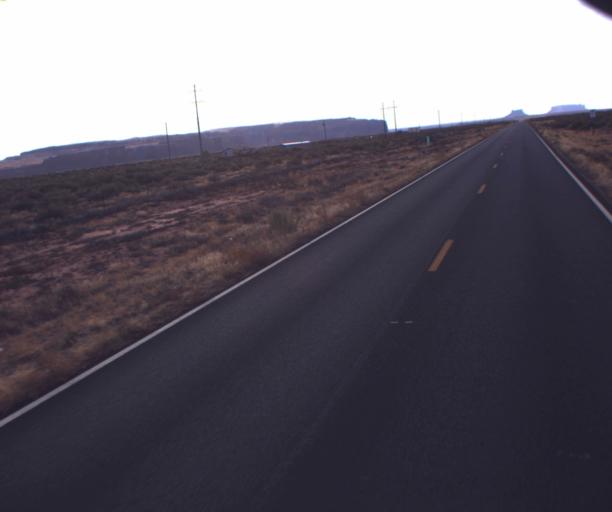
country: US
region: Arizona
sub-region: Apache County
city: Many Farms
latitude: 36.6641
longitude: -109.5969
